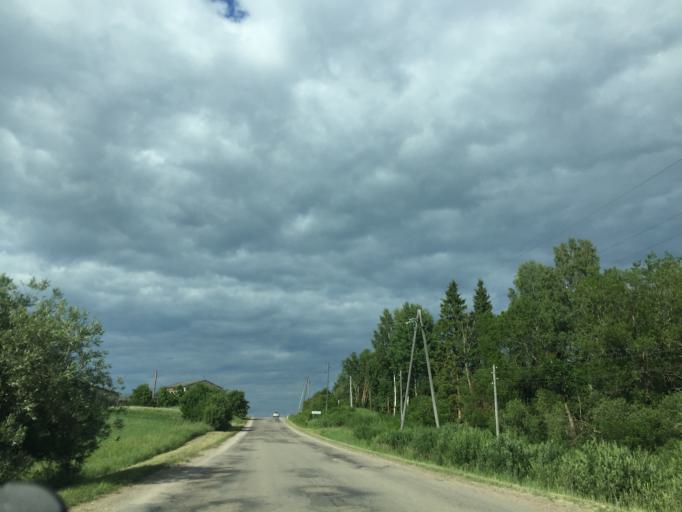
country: LV
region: Skriveri
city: Skriveri
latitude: 56.8409
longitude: 25.1437
